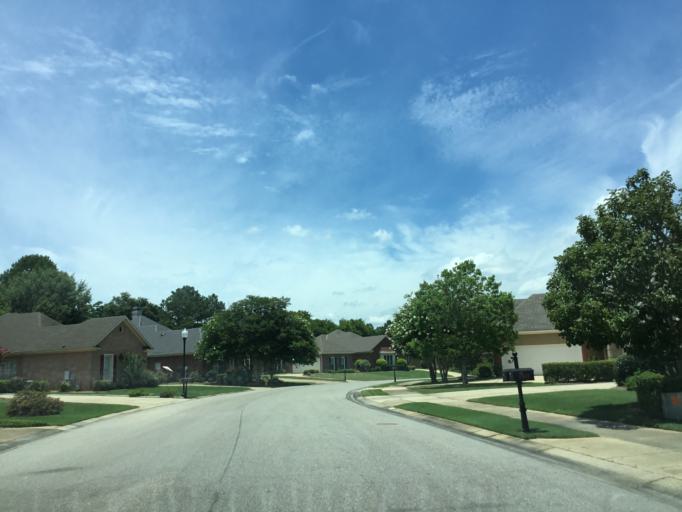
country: US
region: Alabama
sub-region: Montgomery County
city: Pike Road
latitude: 32.3754
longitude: -86.1424
